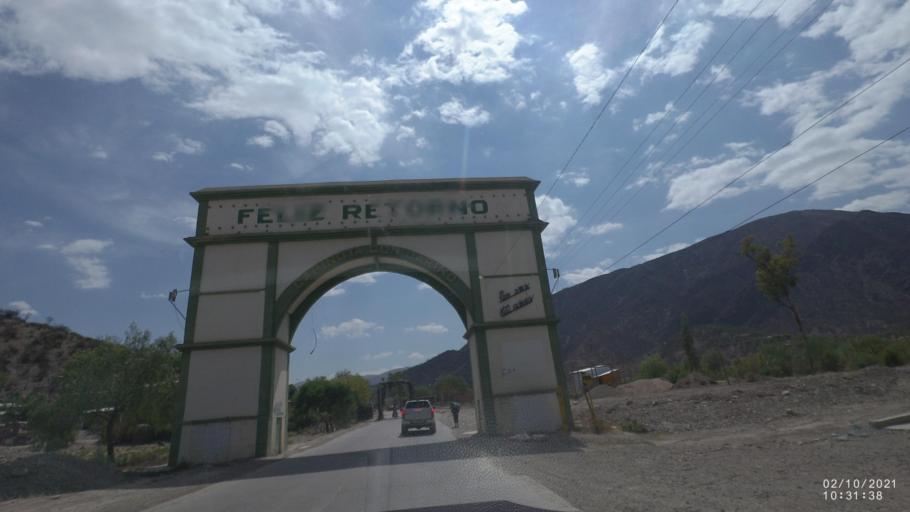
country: BO
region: Cochabamba
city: Capinota
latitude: -17.6937
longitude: -66.2588
